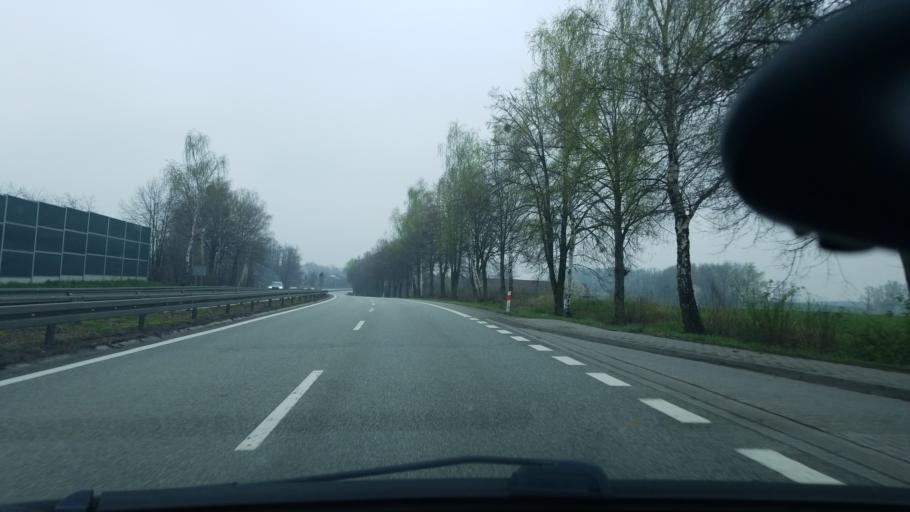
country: PL
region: Silesian Voivodeship
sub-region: Powiat pszczynski
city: Pawlowice
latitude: 49.9829
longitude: 18.7142
